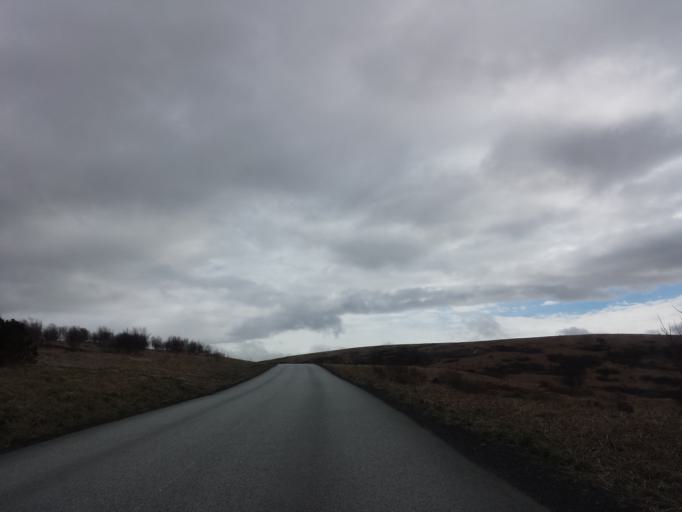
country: IS
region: Capital Region
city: Kopavogur
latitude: 64.0790
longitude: -21.8607
